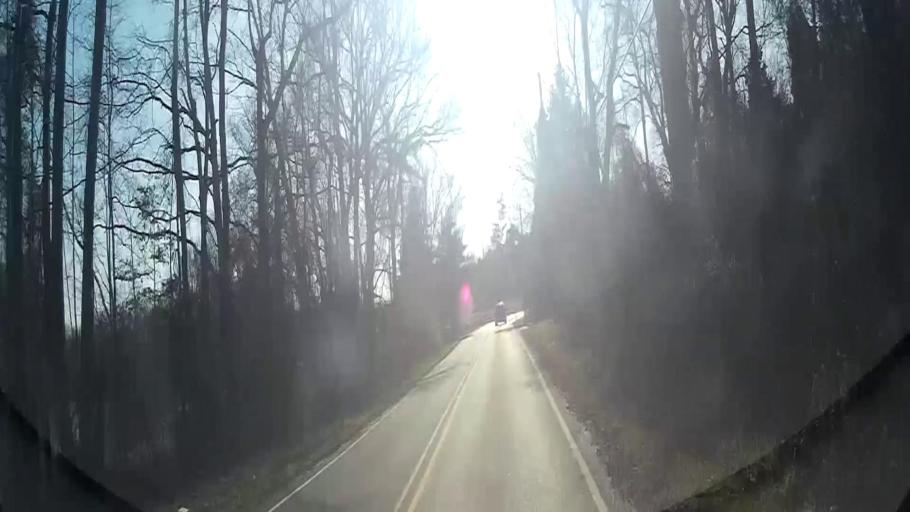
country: US
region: New Jersey
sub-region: Burlington County
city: Marlton
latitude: 39.8528
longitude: -74.9107
